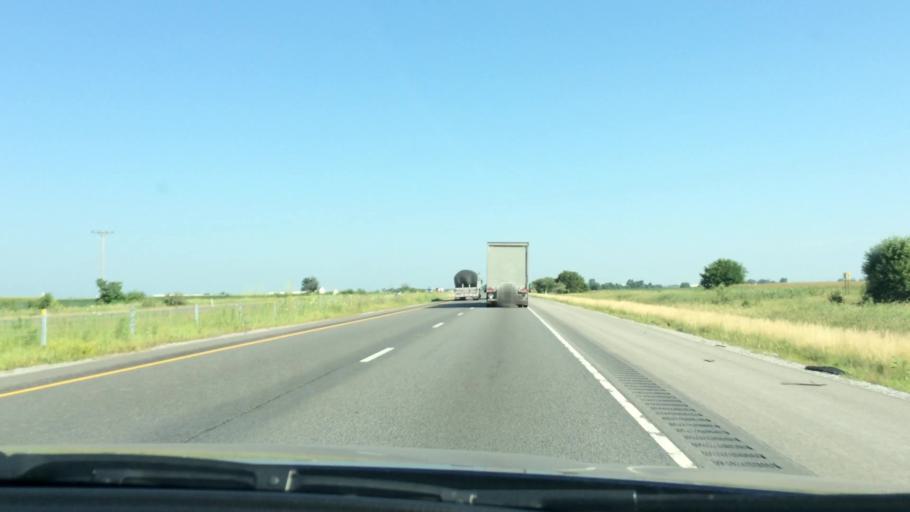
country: US
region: Indiana
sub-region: White County
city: Wolcott
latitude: 40.7358
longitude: -87.0928
